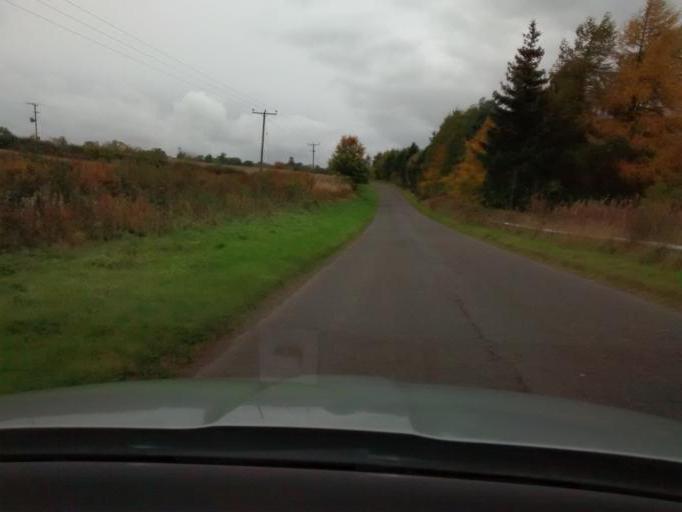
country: GB
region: Scotland
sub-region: Perth and Kinross
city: Auchterarder
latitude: 56.2948
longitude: -3.6881
